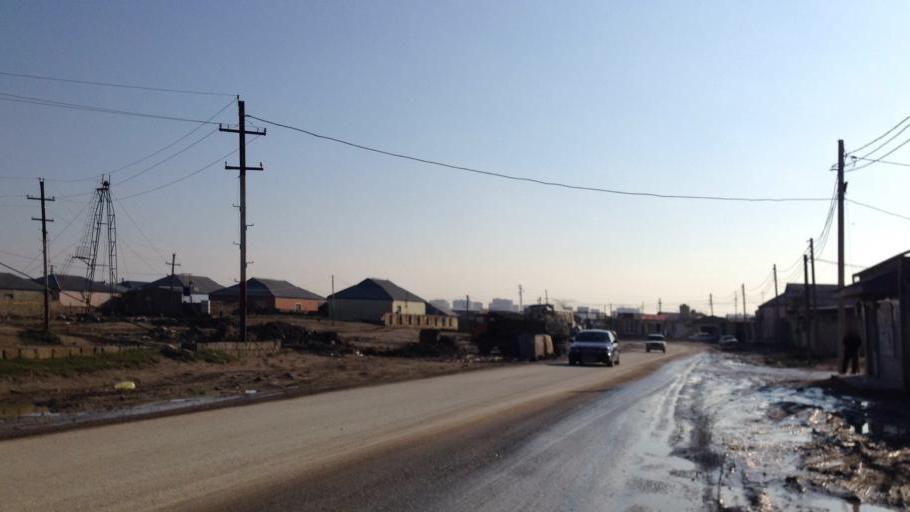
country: AZ
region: Baki
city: Sabuncu
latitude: 40.4497
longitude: 49.9316
